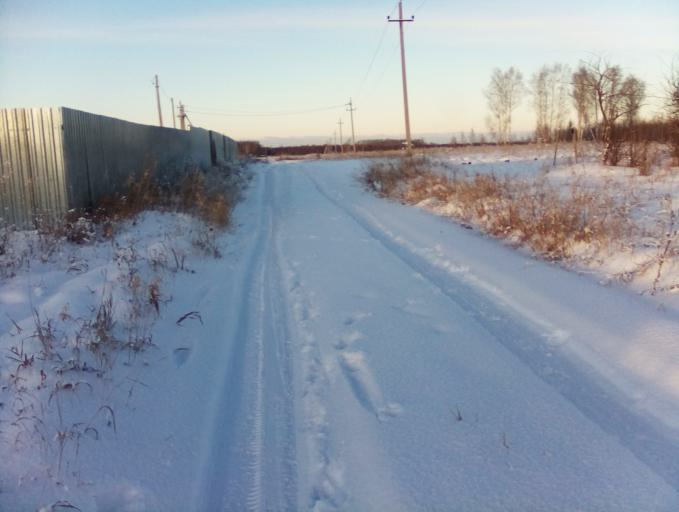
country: RU
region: Chelyabinsk
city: Poletayevo
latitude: 54.9842
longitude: 60.9469
